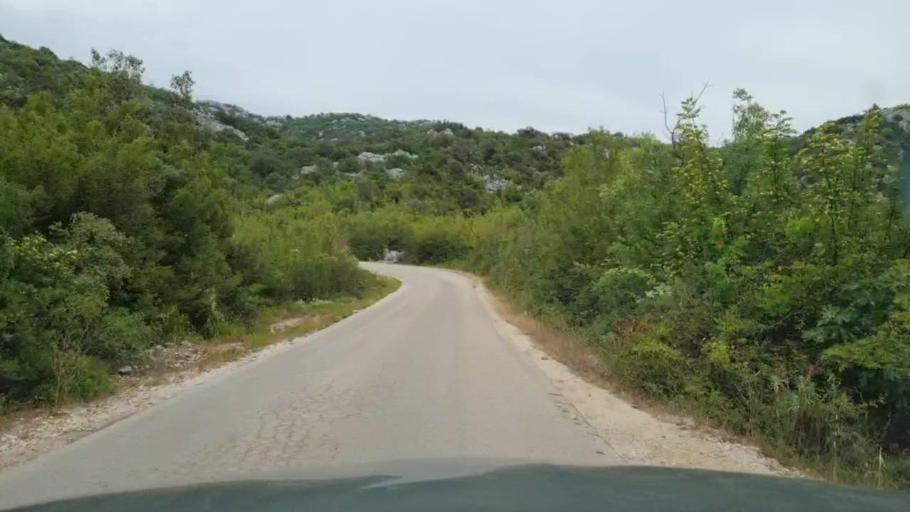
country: BA
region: Federation of Bosnia and Herzegovina
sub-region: Hercegovacko-Bosanski Kanton
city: Neum
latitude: 42.9253
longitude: 17.6832
